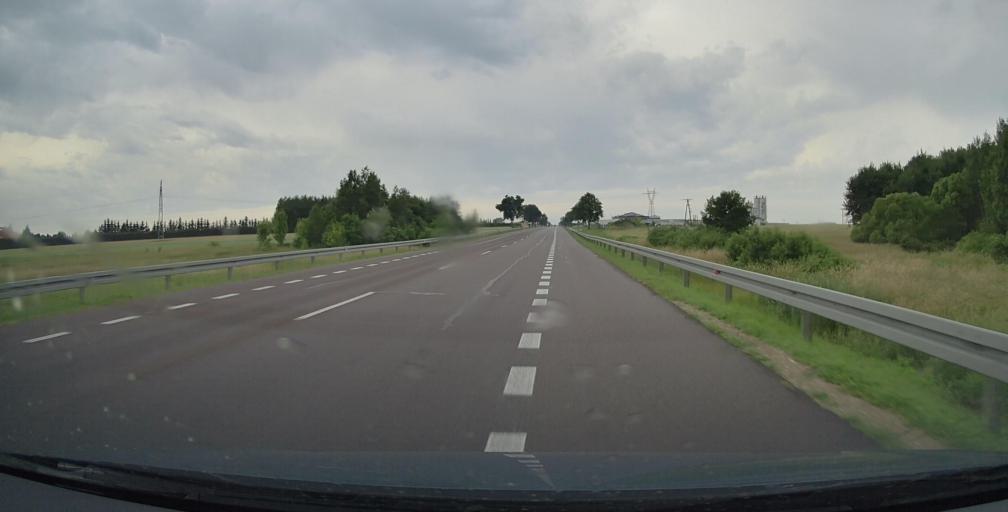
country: PL
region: Lublin Voivodeship
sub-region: Powiat bialski
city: Miedzyrzec Podlaski
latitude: 51.9999
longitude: 22.8022
